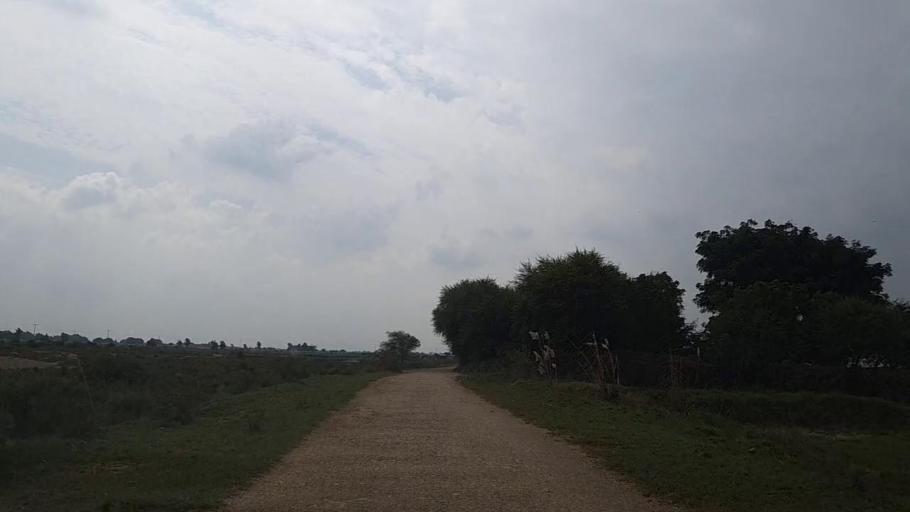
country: PK
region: Sindh
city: Mirpur Batoro
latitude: 24.5881
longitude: 68.1236
